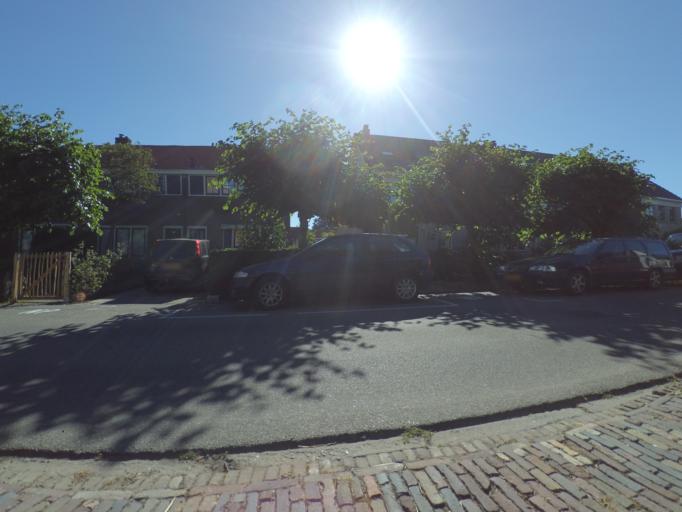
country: NL
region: Utrecht
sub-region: Stichtse Vecht
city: Vreeland
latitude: 52.2307
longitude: 5.0341
